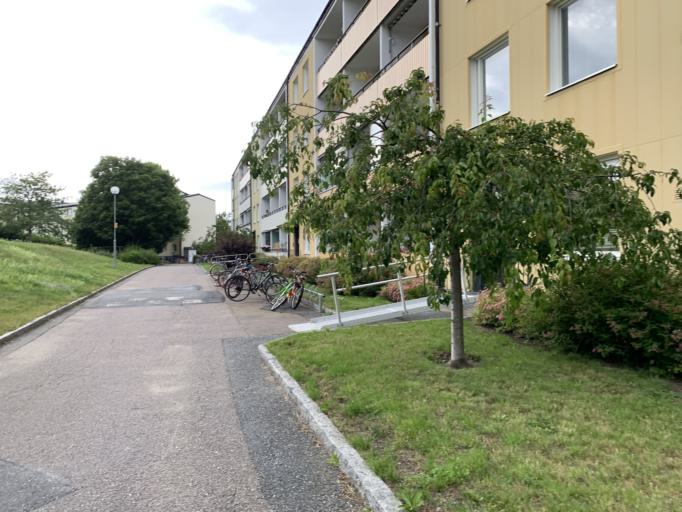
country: SE
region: Stockholm
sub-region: Jarfalla Kommun
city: Jakobsberg
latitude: 59.4225
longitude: 17.8239
